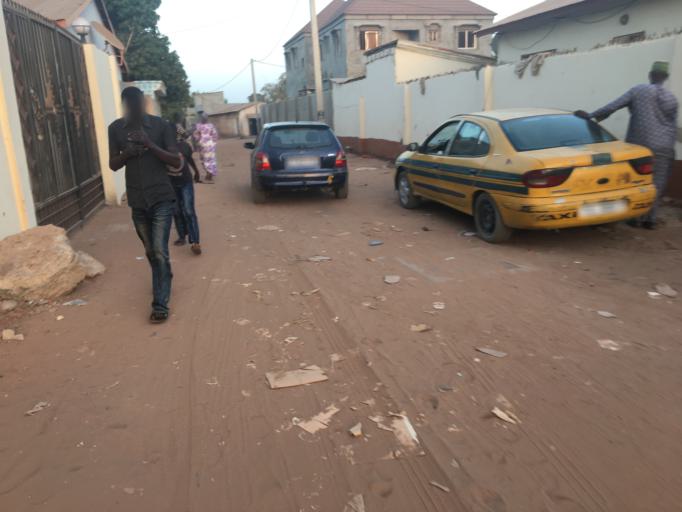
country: GM
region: Western
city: Abuko
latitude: 13.3801
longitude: -16.6809
